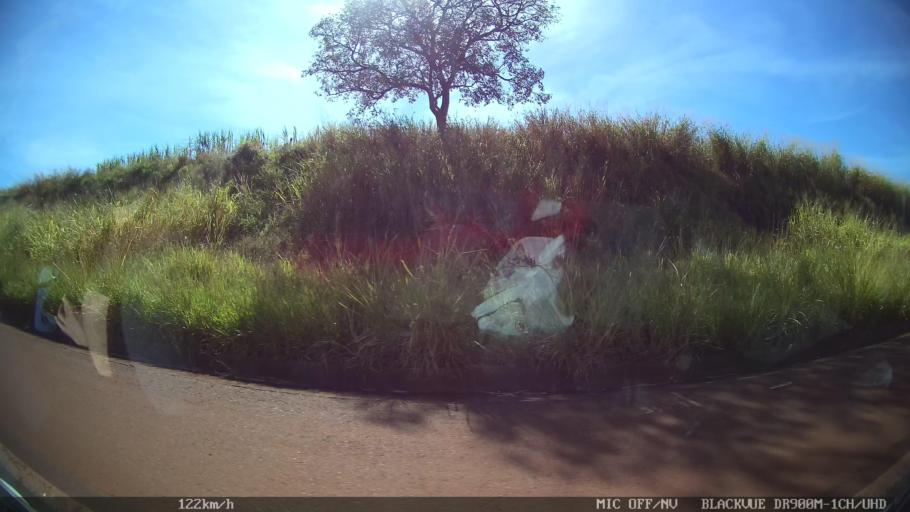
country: BR
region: Sao Paulo
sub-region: Sao Joaquim Da Barra
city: Sao Joaquim da Barra
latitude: -20.5525
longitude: -47.7323
